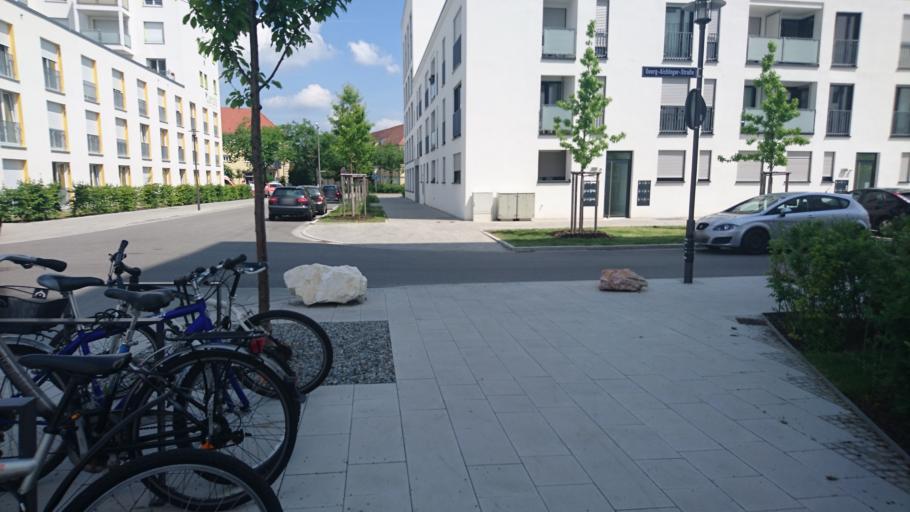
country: DE
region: Bavaria
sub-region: Upper Palatinate
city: Regensburg
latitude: 49.0138
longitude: 12.1228
